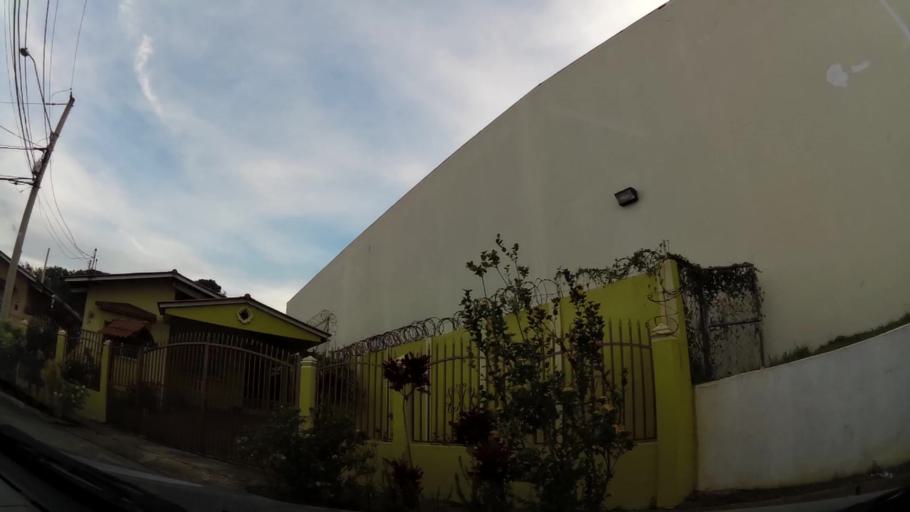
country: PA
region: Panama
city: La Chorrera
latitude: 8.8664
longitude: -79.7641
